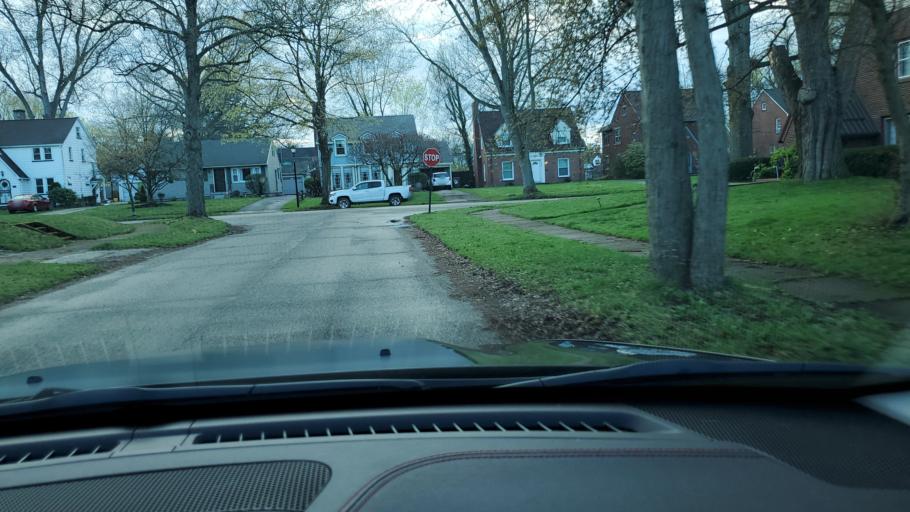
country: US
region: Ohio
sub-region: Mahoning County
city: Boardman
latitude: 41.0569
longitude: -80.6609
